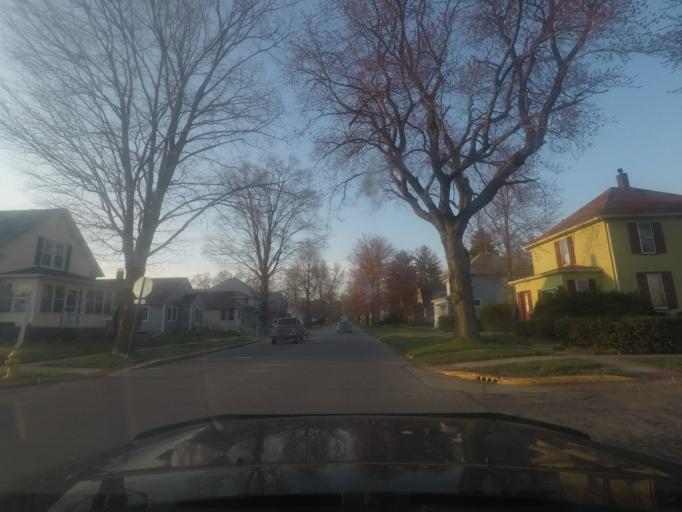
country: US
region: Indiana
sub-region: LaPorte County
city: LaPorte
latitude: 41.6020
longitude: -86.7291
